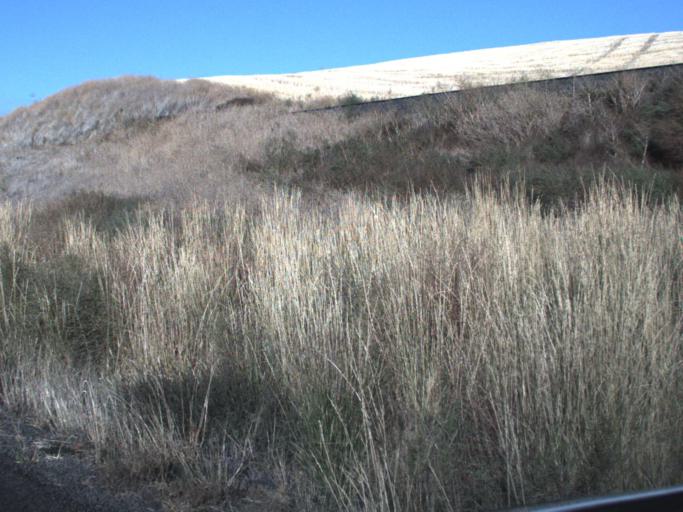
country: US
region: Washington
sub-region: Walla Walla County
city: Walla Walla
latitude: 46.1592
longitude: -118.3794
